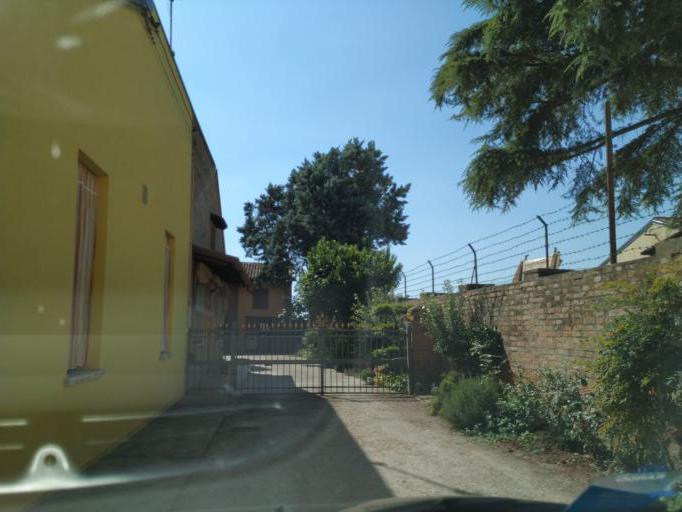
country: IT
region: Emilia-Romagna
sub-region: Provincia di Ferrara
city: Coccanile-Cesta
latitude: 44.9122
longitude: 11.9111
